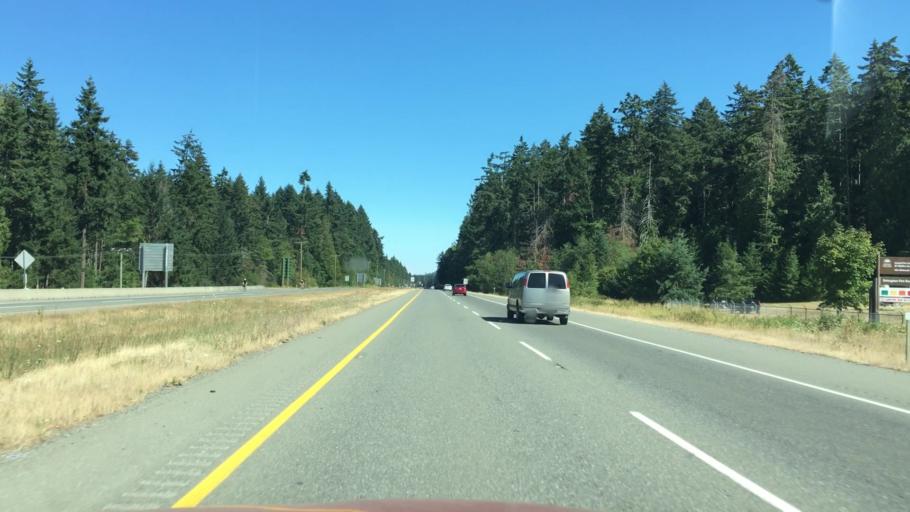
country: CA
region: British Columbia
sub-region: Regional District of Nanaimo
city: Parksville
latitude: 49.3037
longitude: -124.3121
